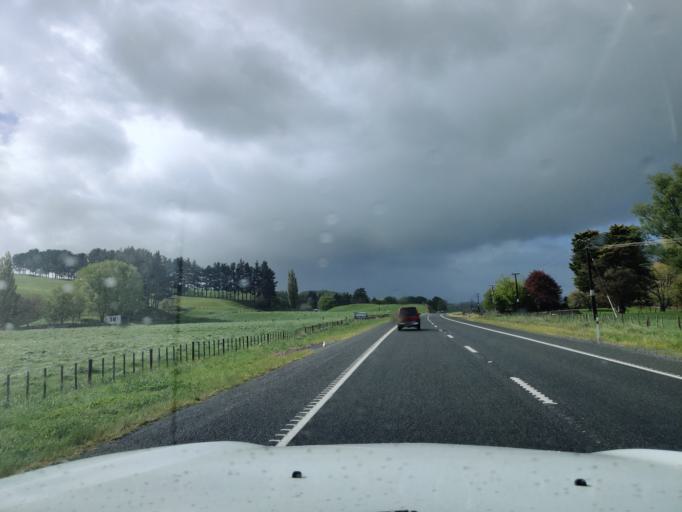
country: NZ
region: Waikato
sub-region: Matamata-Piako District
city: Matamata
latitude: -37.9583
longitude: 175.6857
